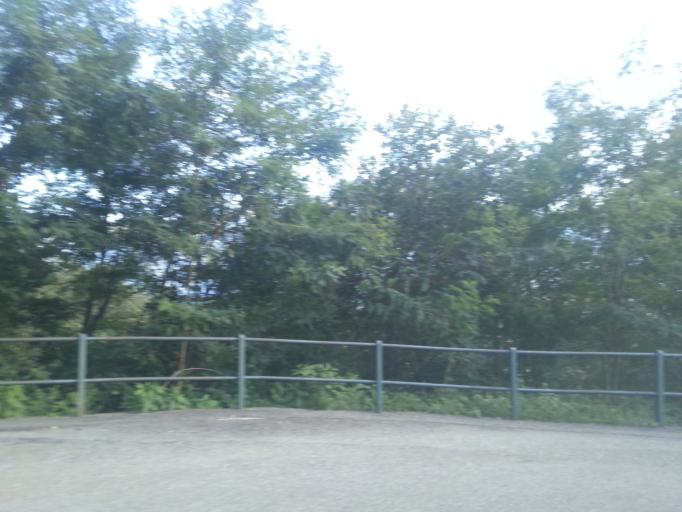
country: IT
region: Lombardy
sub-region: Provincia di Como
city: Sorico
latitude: 46.1803
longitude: 9.3861
